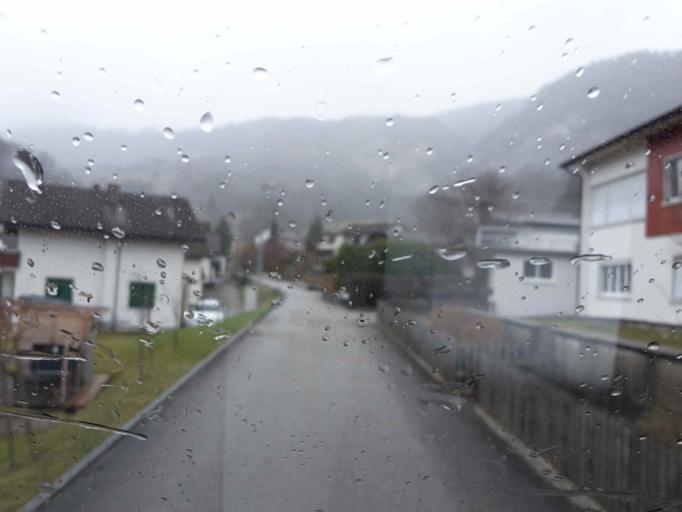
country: CH
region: Solothurn
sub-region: Bezirk Thal
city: Welschenrohr
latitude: 47.2817
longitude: 7.5244
